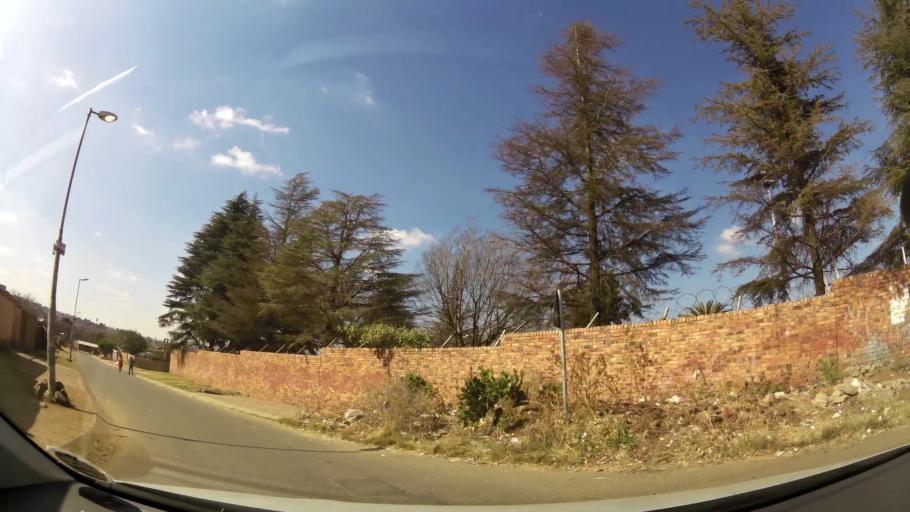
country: ZA
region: Gauteng
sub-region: City of Johannesburg Metropolitan Municipality
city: Soweto
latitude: -26.2466
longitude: 27.8834
